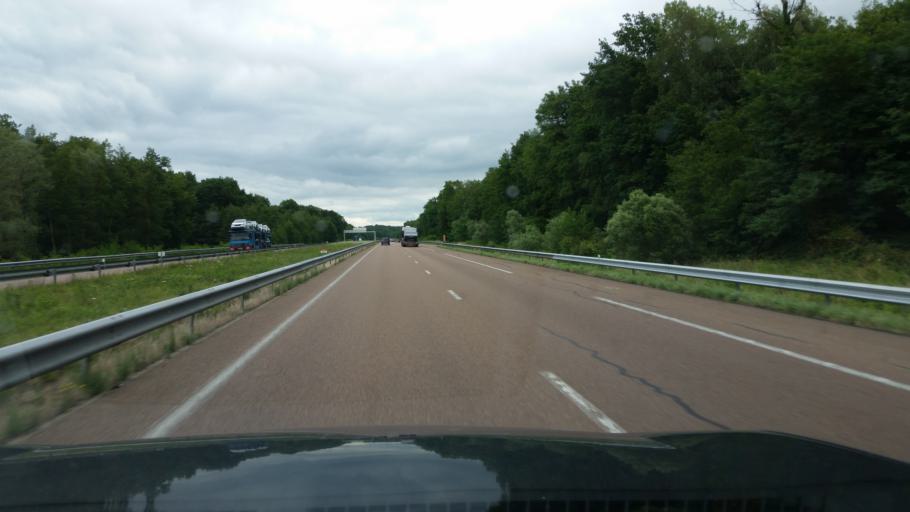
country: FR
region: Franche-Comte
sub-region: Departement du Jura
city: Bletterans
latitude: 46.6800
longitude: 5.4383
